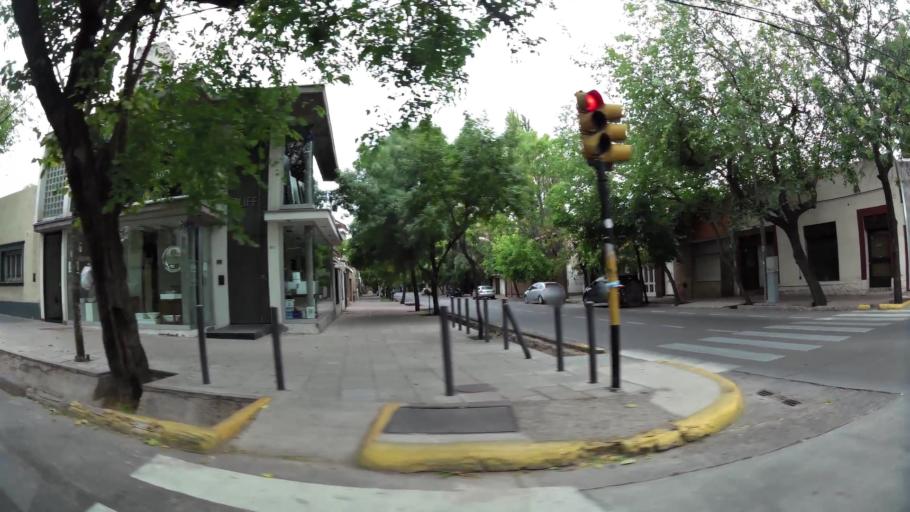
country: AR
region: Mendoza
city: Mendoza
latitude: -32.8946
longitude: -68.8376
